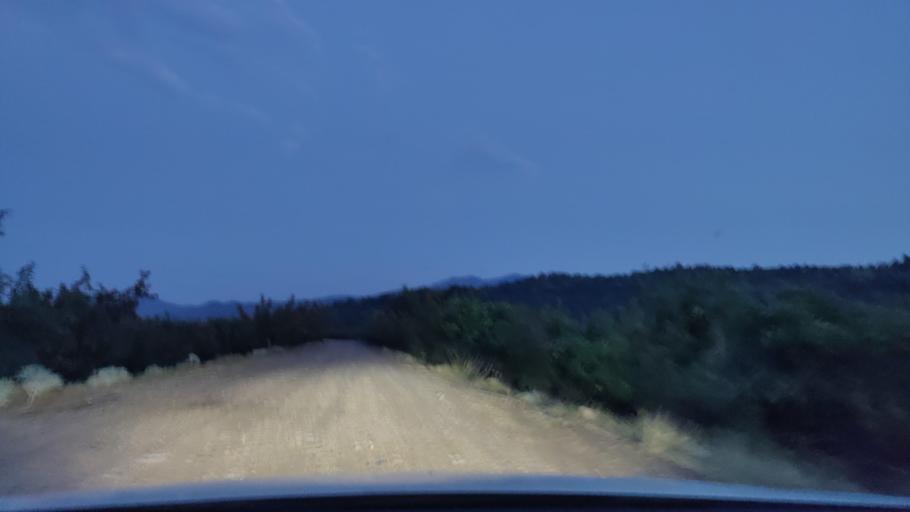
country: GR
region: Central Macedonia
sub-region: Nomos Serron
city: Chrysochorafa
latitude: 41.2023
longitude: 23.0808
